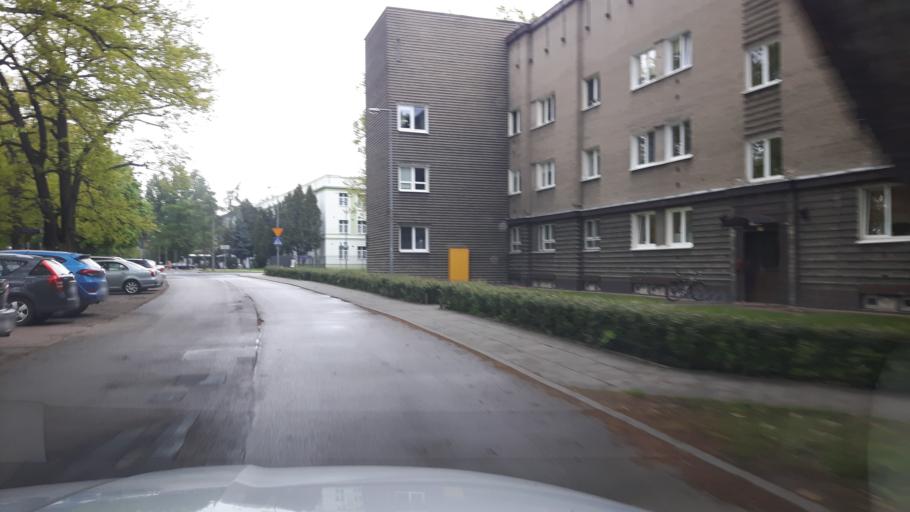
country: PL
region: Masovian Voivodeship
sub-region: Warszawa
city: Rembertow
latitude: 52.2680
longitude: 21.1791
